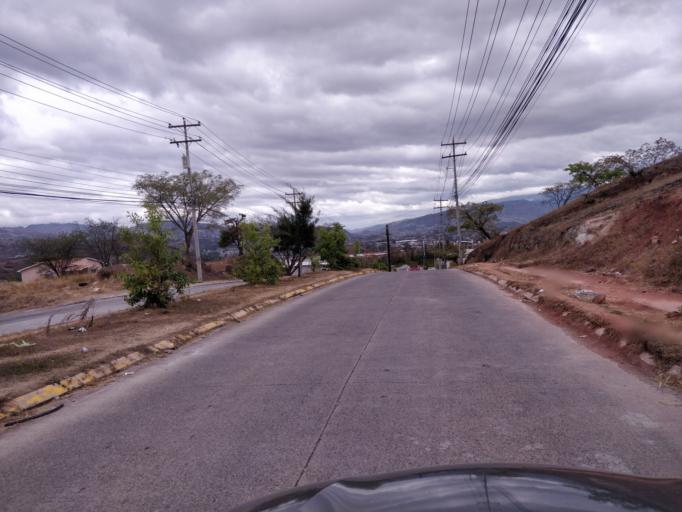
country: HN
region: Francisco Morazan
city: Yaguacire
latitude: 14.0401
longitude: -87.2369
